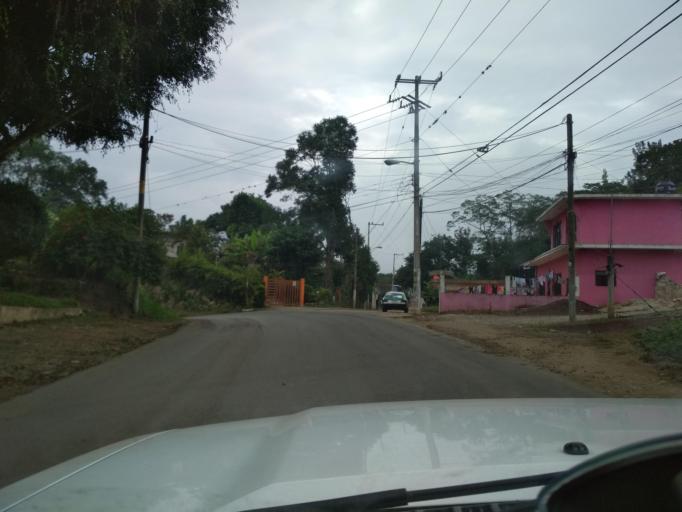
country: MX
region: Veracruz
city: El Castillo
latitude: 19.5634
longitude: -96.8598
